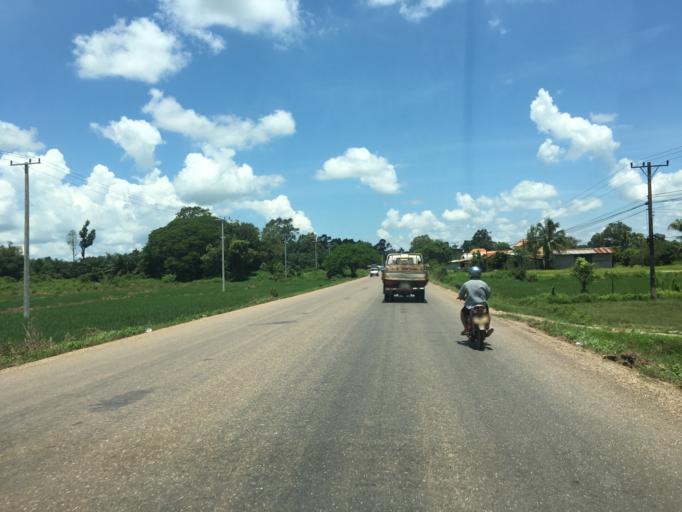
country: LA
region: Vientiane
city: Vientiane
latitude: 18.1282
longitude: 102.5050
